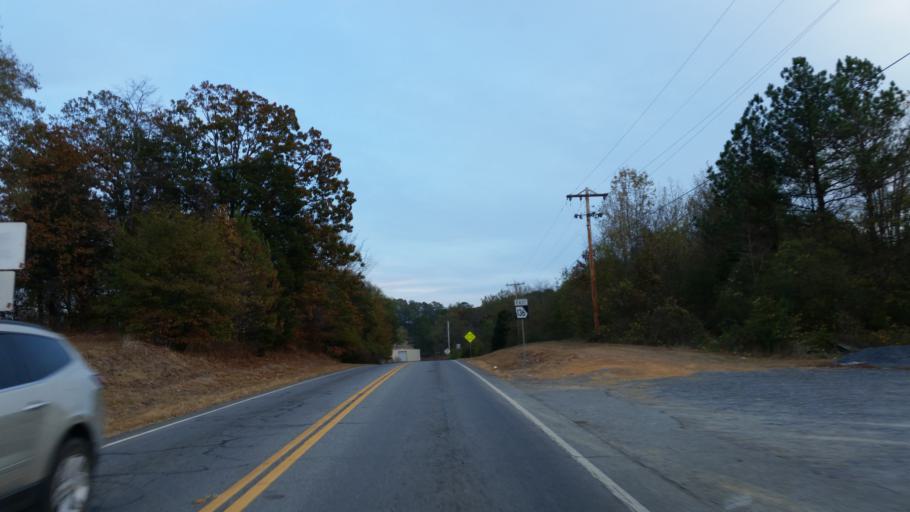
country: US
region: Georgia
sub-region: Gordon County
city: Calhoun
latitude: 34.6014
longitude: -84.8661
